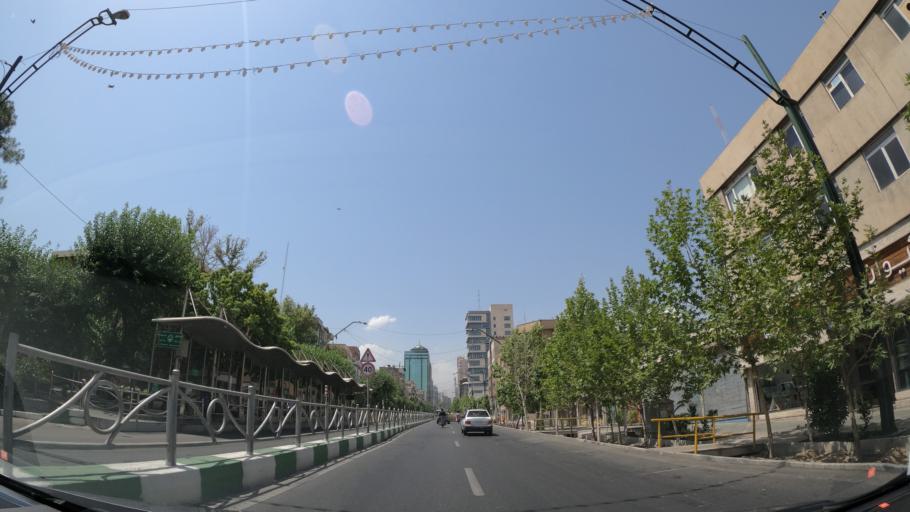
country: IR
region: Tehran
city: Tehran
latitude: 35.7285
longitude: 51.4130
